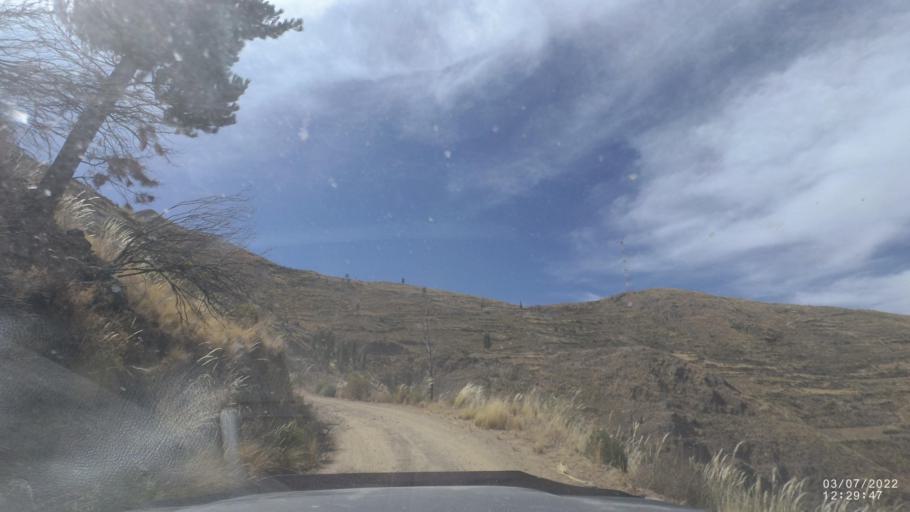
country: BO
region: Cochabamba
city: Irpa Irpa
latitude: -17.8107
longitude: -66.6102
